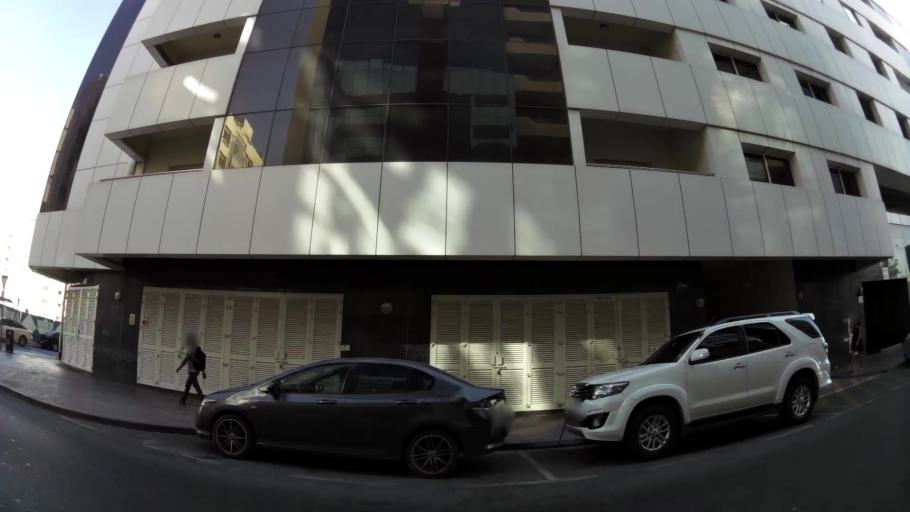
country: AE
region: Ash Shariqah
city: Sharjah
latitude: 25.2648
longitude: 55.3261
